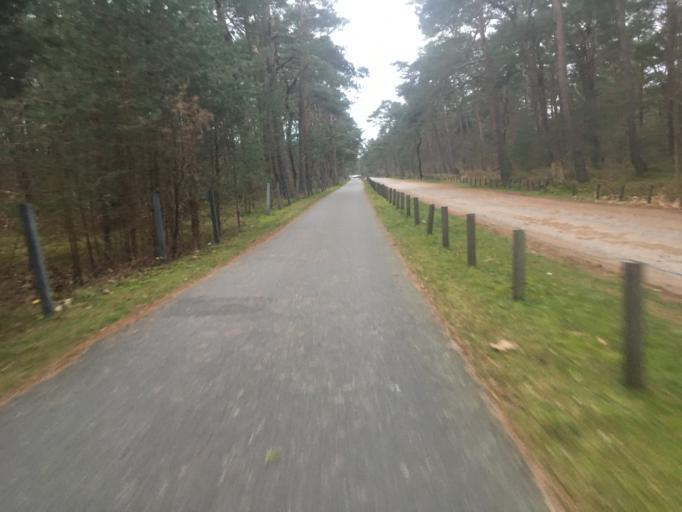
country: DE
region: Mecklenburg-Vorpommern
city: Sagard
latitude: 54.4690
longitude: 13.5677
